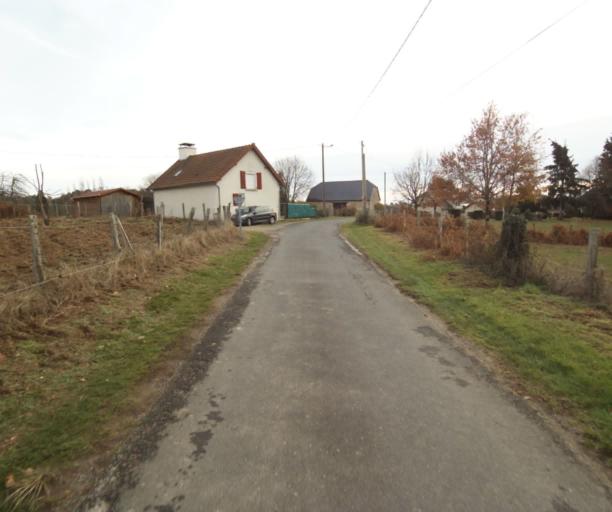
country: FR
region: Limousin
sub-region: Departement de la Correze
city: Saint-Mexant
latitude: 45.2626
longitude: 1.6466
